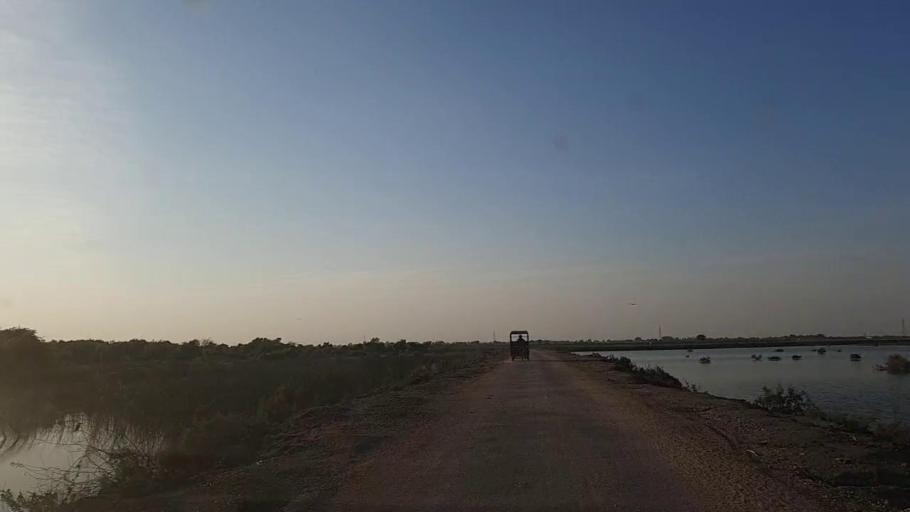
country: PK
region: Sindh
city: Mirpur Batoro
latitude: 24.6862
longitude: 68.2053
